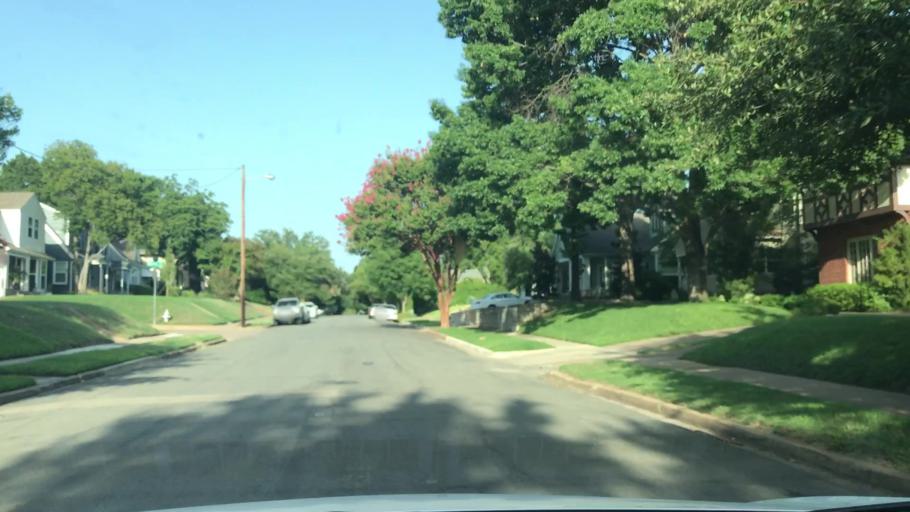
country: US
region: Texas
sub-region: Dallas County
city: Highland Park
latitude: 32.8221
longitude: -96.7586
